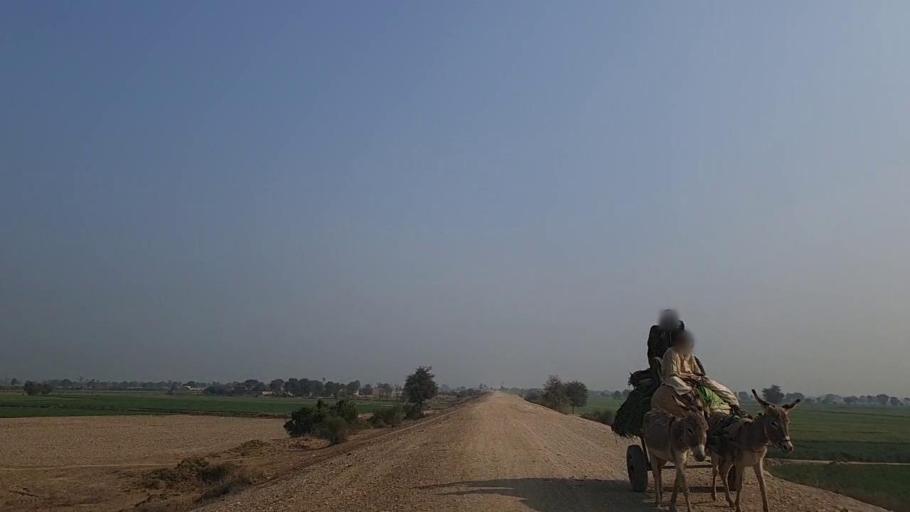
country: PK
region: Sindh
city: Sann
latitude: 26.0930
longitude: 68.1484
